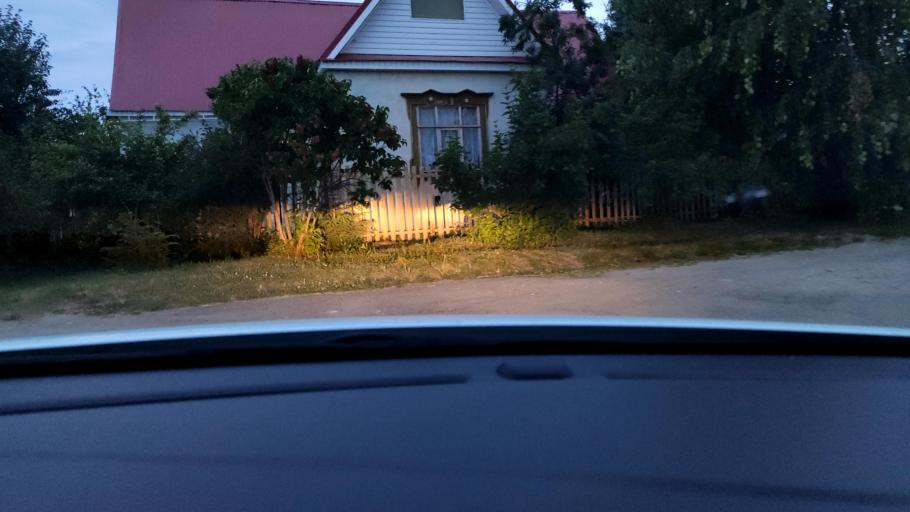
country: RU
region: Tatarstan
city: Stolbishchi
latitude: 55.7427
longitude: 49.2681
